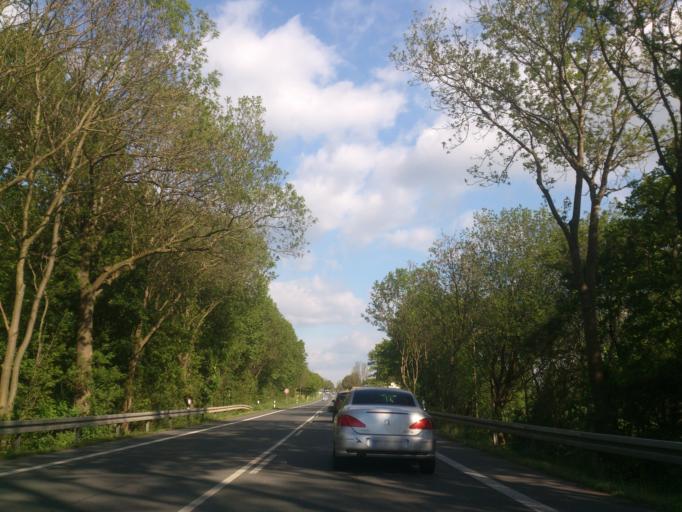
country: DE
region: North Rhine-Westphalia
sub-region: Regierungsbezirk Detmold
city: Paderborn
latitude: 51.6795
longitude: 8.8258
